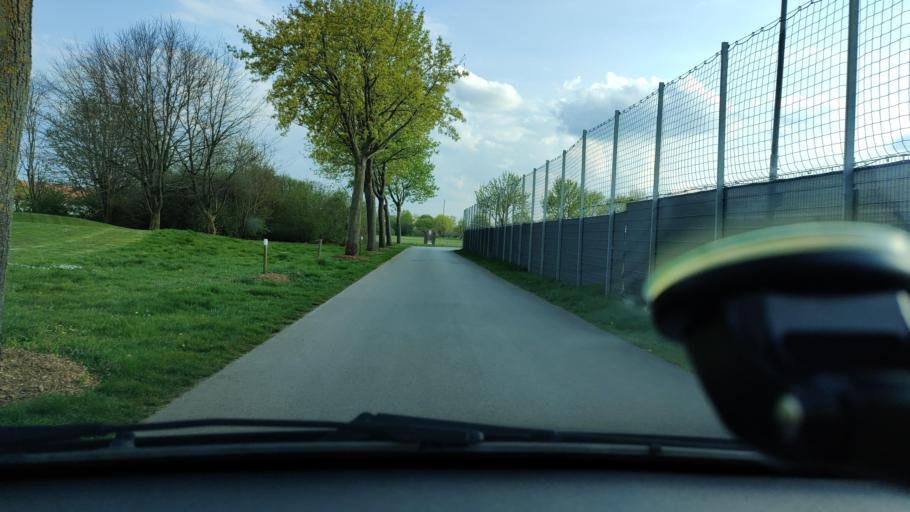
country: DE
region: North Rhine-Westphalia
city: Rees
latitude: 51.7464
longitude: 6.3589
